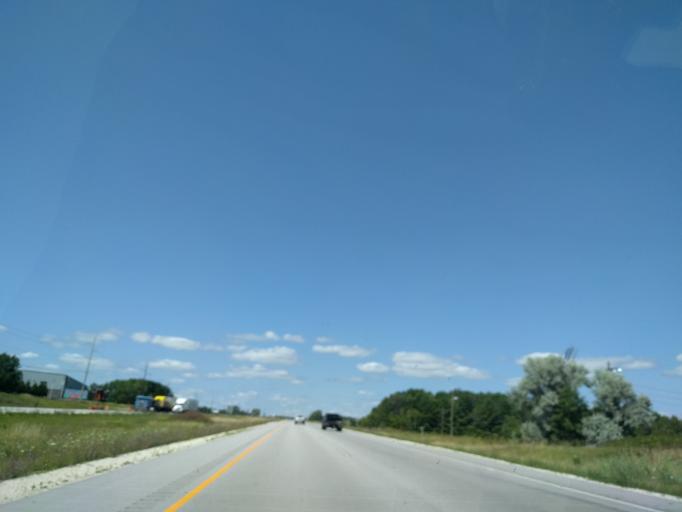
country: US
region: Wisconsin
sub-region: Manitowoc County
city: Manitowoc
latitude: 44.0782
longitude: -87.7169
